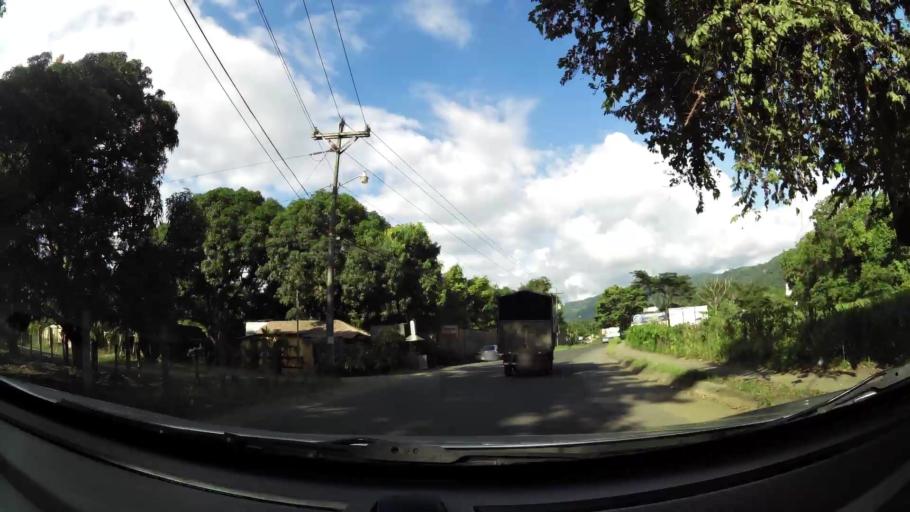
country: CR
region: Puntarenas
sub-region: Canton de Garabito
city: Jaco
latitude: 9.6594
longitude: -84.6413
